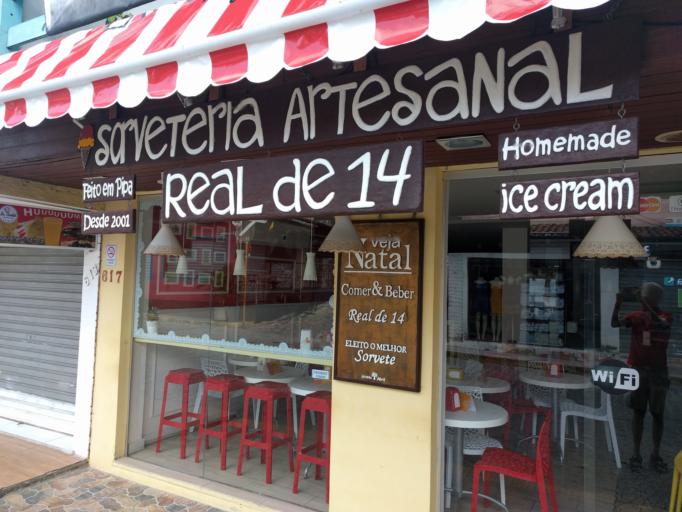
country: BR
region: Rio Grande do Norte
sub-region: Ares
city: Ares
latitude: -6.2285
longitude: -35.0506
